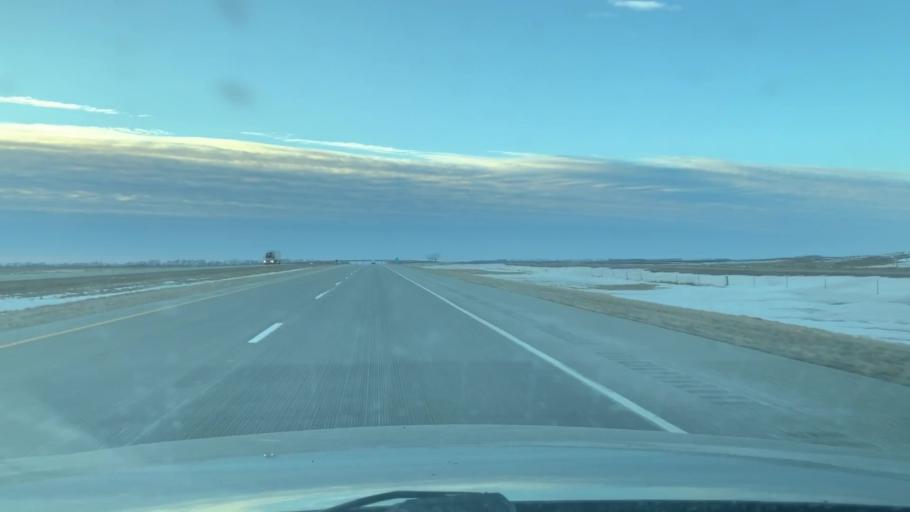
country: US
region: North Dakota
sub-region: Cass County
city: Casselton
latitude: 46.8758
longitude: -97.4777
